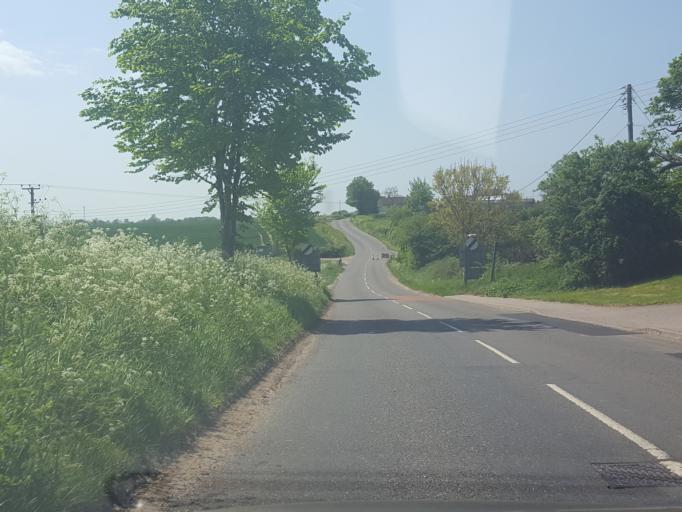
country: GB
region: England
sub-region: Essex
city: Great Bentley
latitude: 51.8552
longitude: 1.0547
